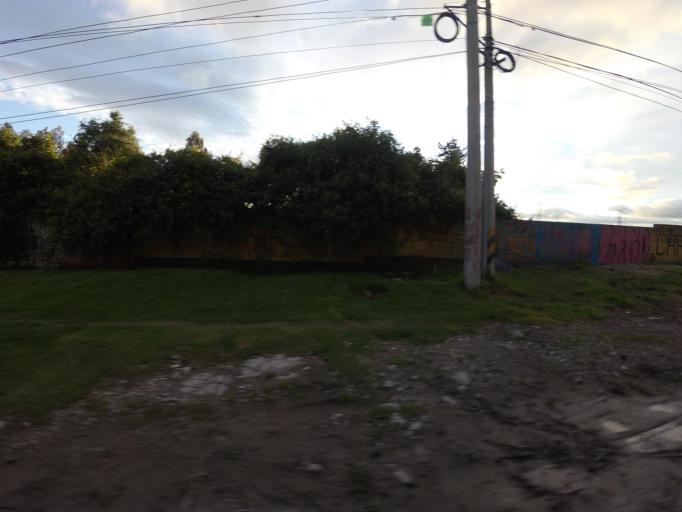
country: CO
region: Cundinamarca
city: La Calera
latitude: 4.7743
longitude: -74.0262
